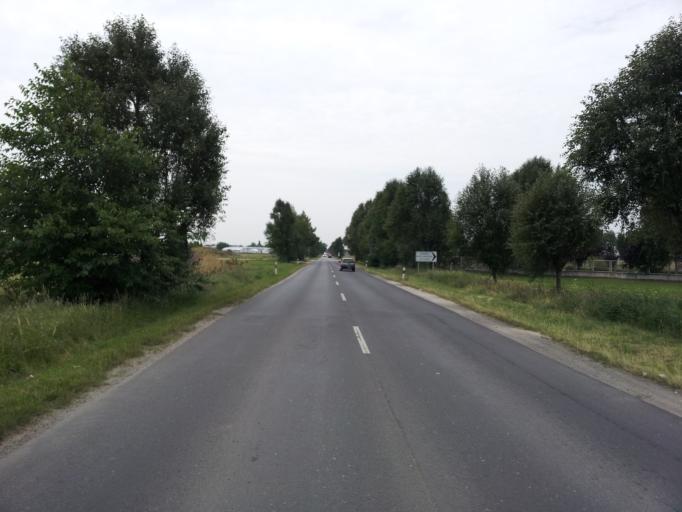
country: HU
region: Pest
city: Szigetszentmiklos
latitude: 47.3688
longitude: 19.0483
